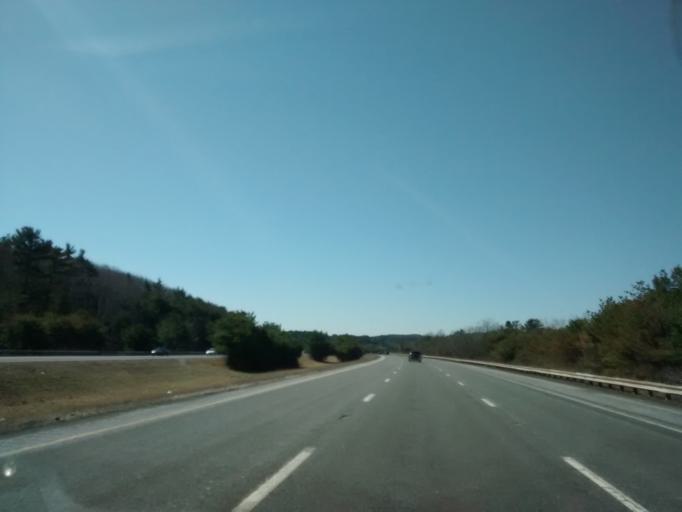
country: US
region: Massachusetts
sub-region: Worcester County
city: Sturbridge
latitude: 42.1064
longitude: -72.0840
